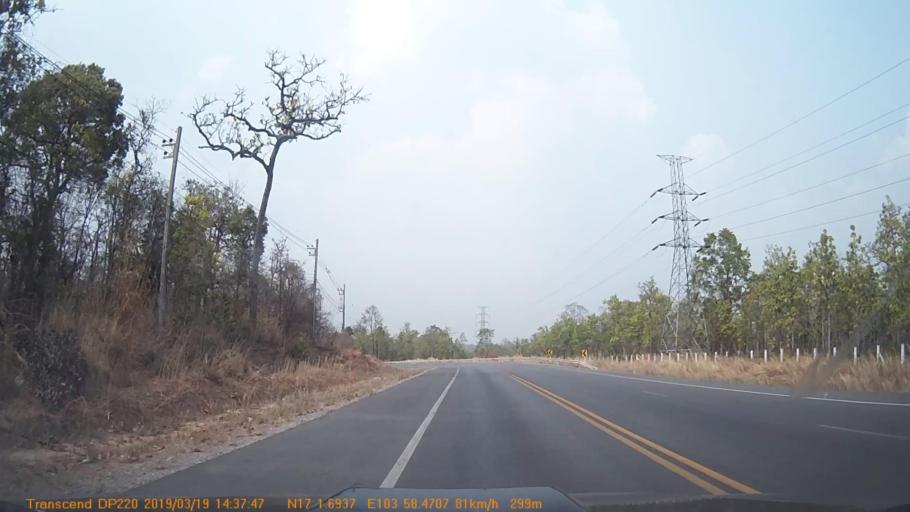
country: TH
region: Sakon Nakhon
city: Phu Phan
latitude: 17.0285
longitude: 103.9745
